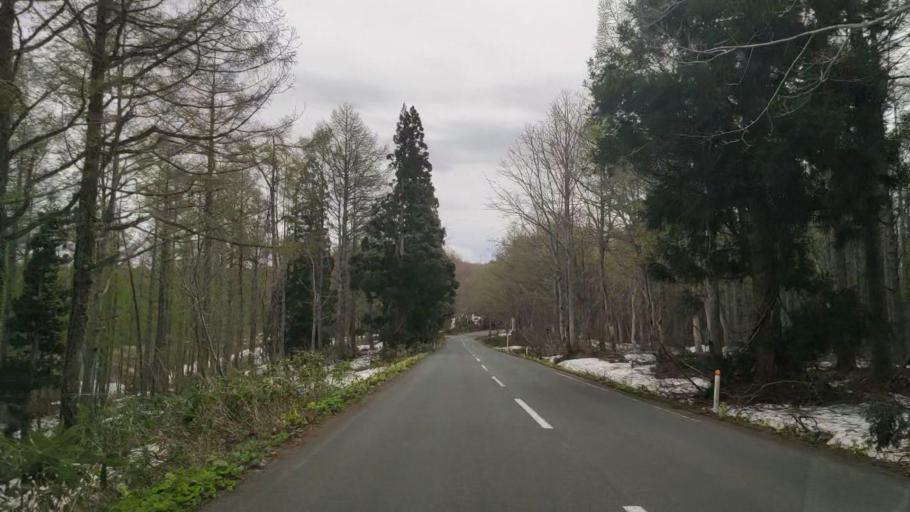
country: JP
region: Aomori
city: Aomori Shi
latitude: 40.7198
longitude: 140.8602
